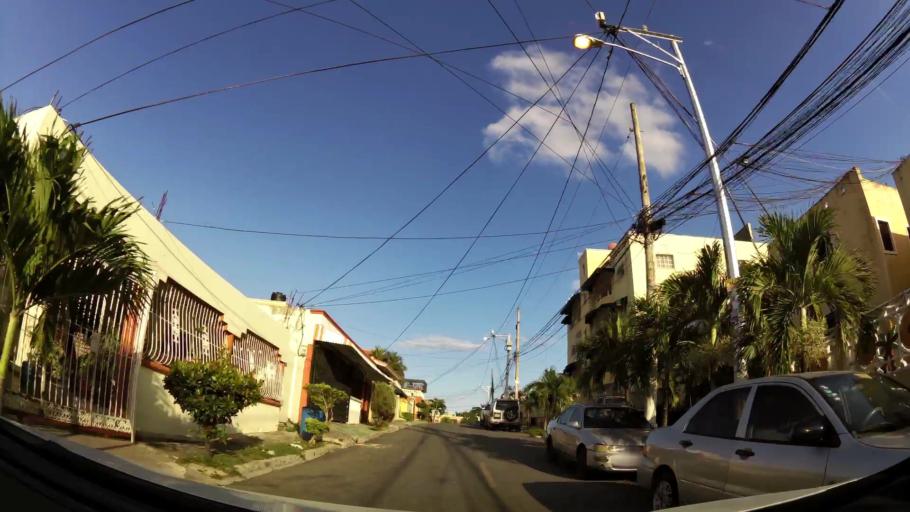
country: DO
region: Nacional
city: Ensanche Luperon
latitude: 18.5462
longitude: -69.9060
